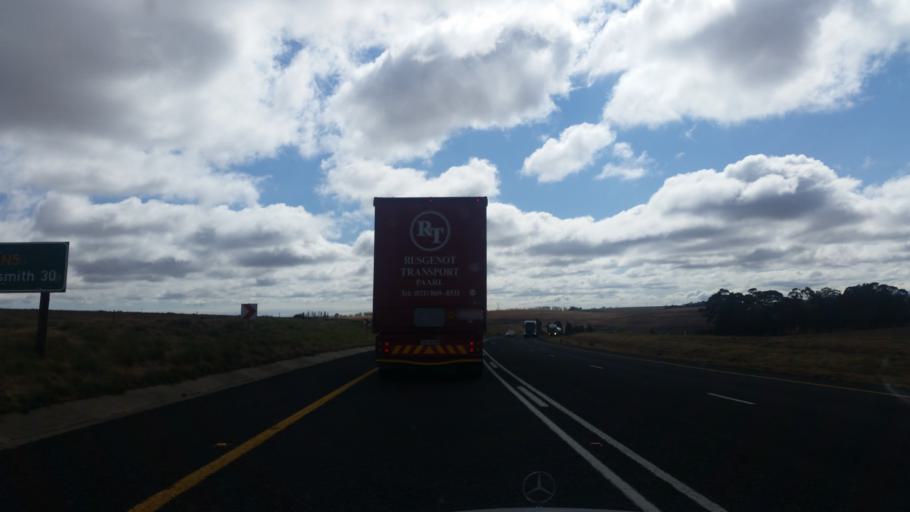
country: ZA
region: Orange Free State
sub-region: Thabo Mofutsanyana District Municipality
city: Phuthaditjhaba
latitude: -28.2732
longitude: 28.8496
